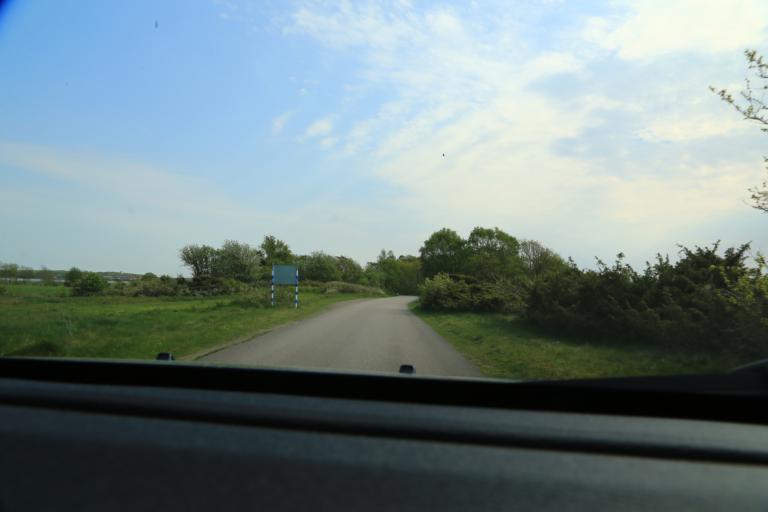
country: SE
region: Halland
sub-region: Varbergs Kommun
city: Varberg
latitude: 57.1438
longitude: 12.2273
